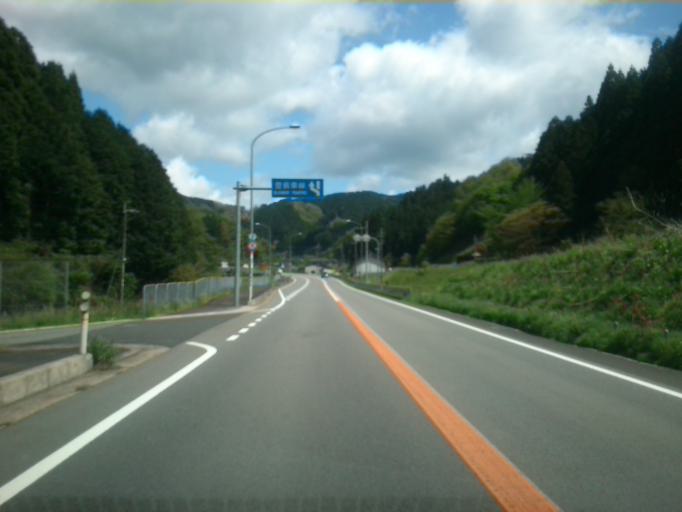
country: JP
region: Kyoto
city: Fukuchiyama
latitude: 35.4194
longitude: 135.0324
